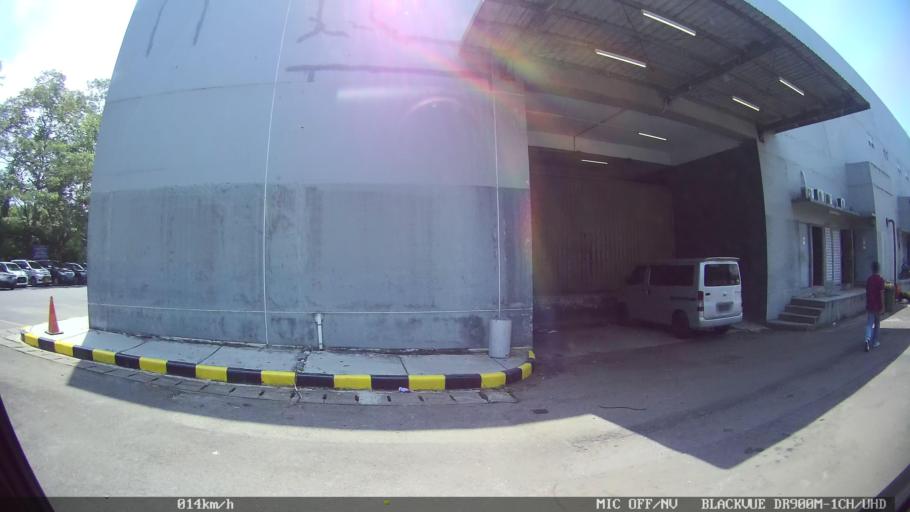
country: ID
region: Lampung
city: Kedaton
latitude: -5.3714
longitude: 105.2379
